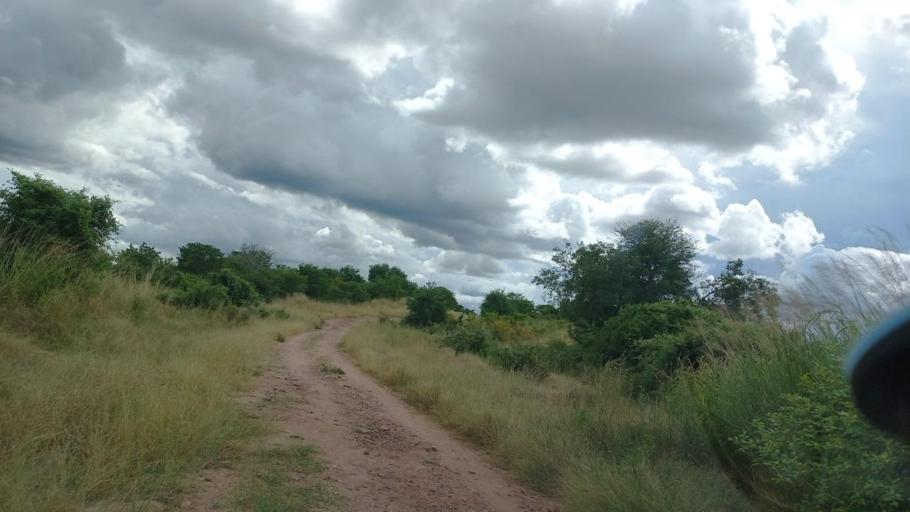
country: ZM
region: Lusaka
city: Luangwa
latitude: -15.6410
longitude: 30.3833
